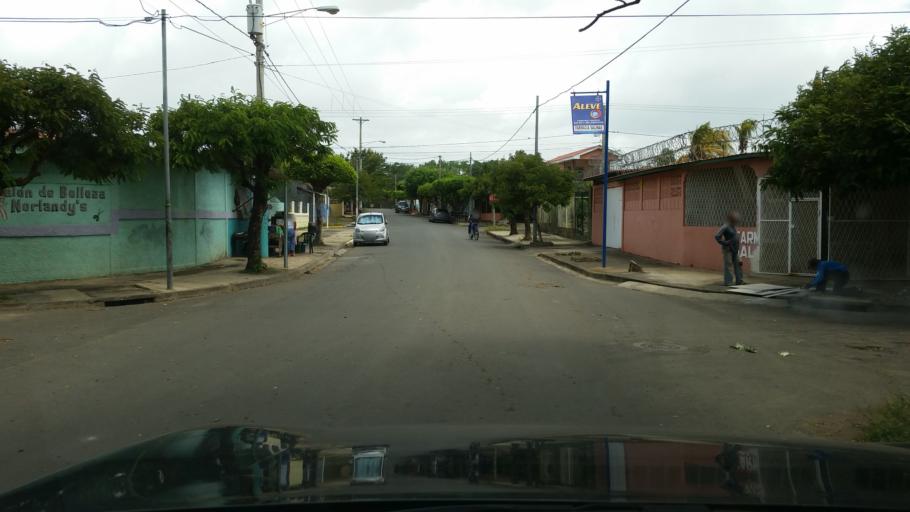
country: NI
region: Managua
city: Managua
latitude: 12.1360
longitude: -86.2139
